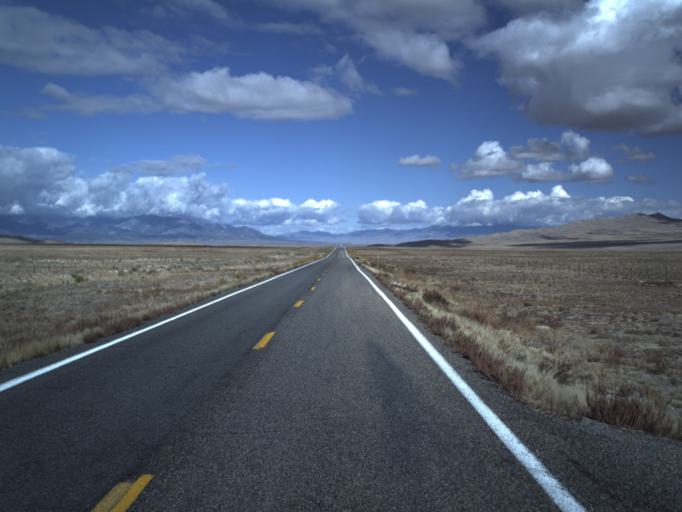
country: US
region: Utah
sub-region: Beaver County
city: Milford
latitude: 38.6623
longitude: -113.8782
